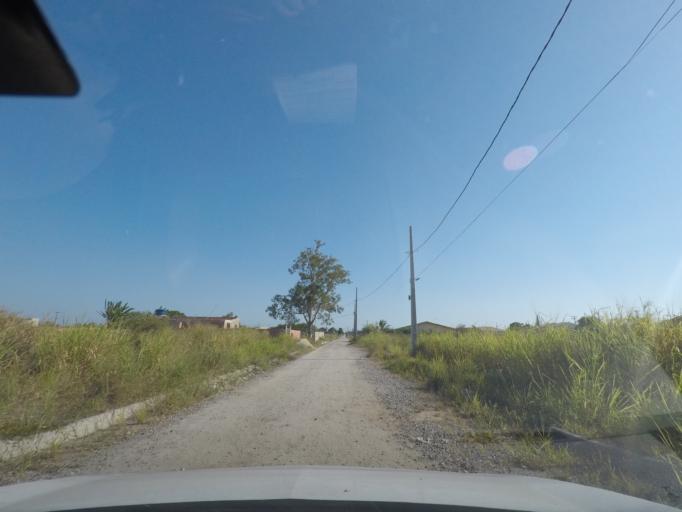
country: BR
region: Rio de Janeiro
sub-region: Marica
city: Marica
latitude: -22.9593
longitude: -42.9263
